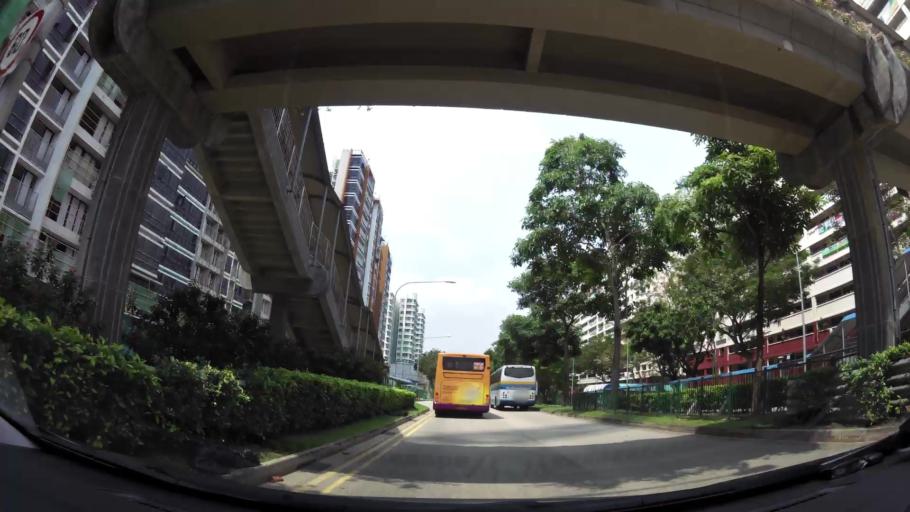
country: MY
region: Johor
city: Kampung Pasir Gudang Baru
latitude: 1.3724
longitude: 103.9467
